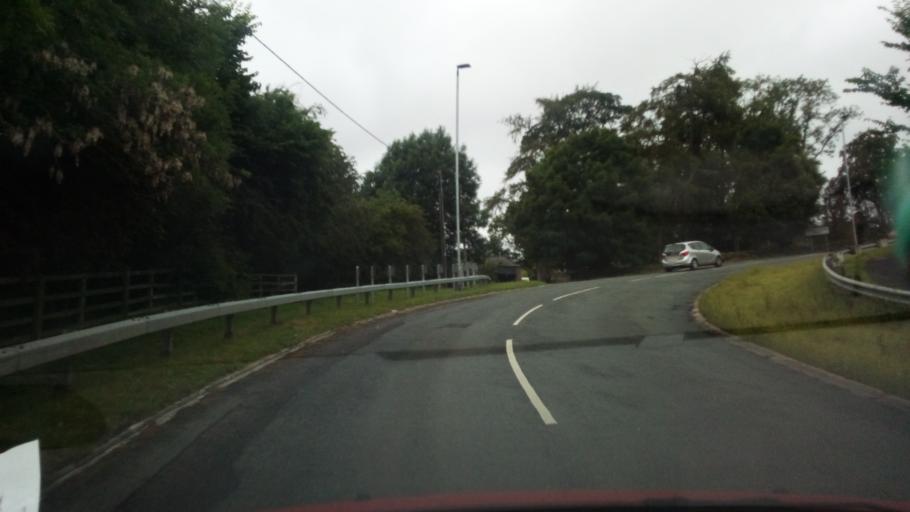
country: GB
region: England
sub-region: County Durham
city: Stanhope
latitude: 54.7551
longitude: -2.0158
